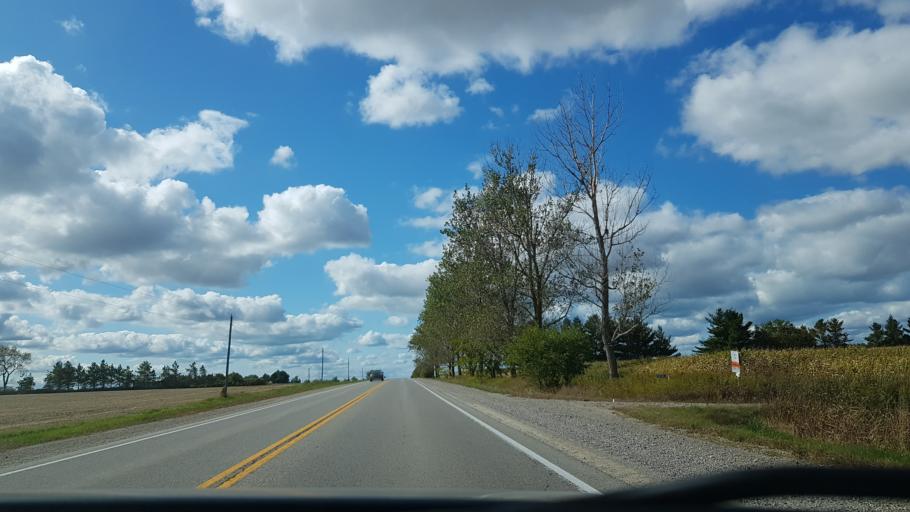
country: CA
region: Ontario
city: South Huron
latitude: 43.3521
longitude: -81.5762
